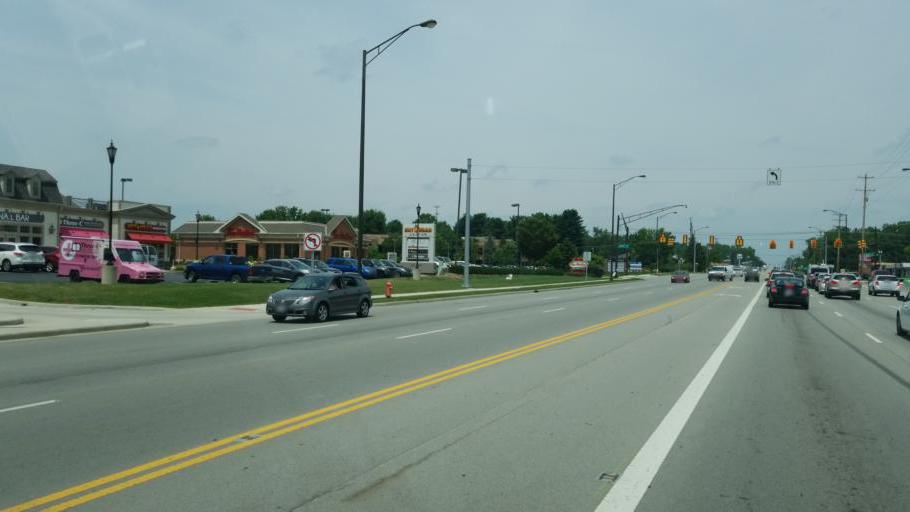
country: US
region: Ohio
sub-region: Franklin County
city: Worthington
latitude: 40.1345
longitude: -83.0168
